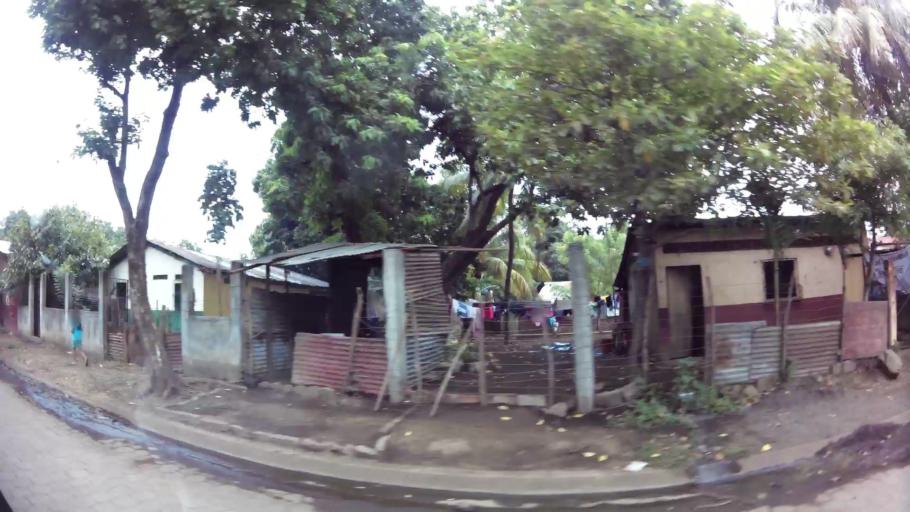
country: NI
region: Chinandega
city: Chinandega
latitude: 12.6148
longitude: -87.1143
